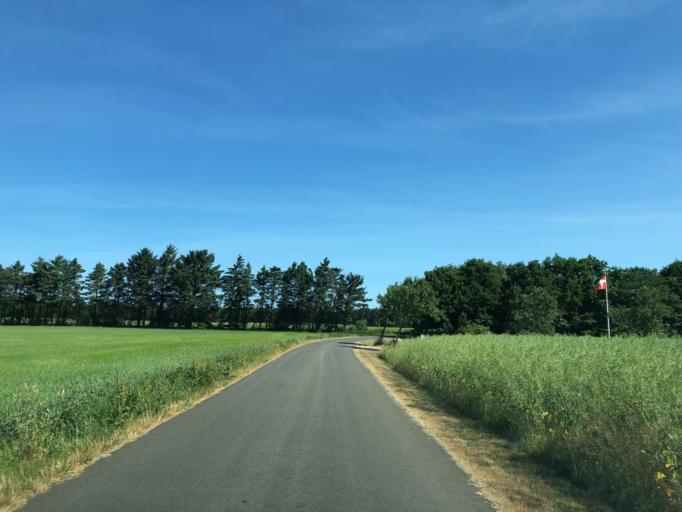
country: DK
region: Central Jutland
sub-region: Struer Kommune
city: Struer
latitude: 56.4281
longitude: 8.4390
